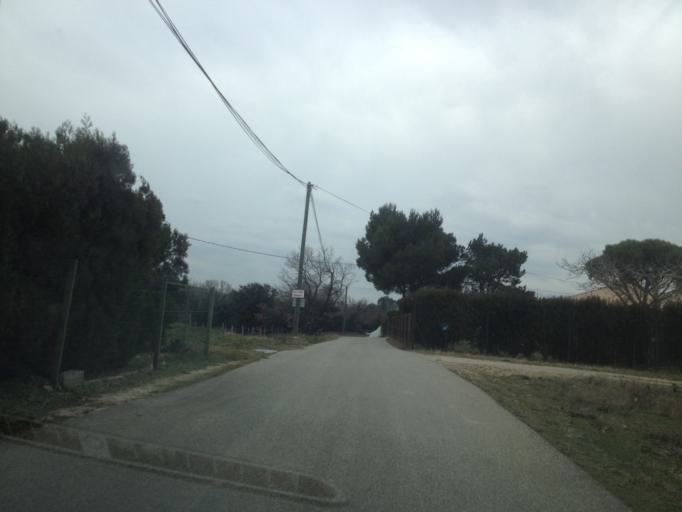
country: FR
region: Provence-Alpes-Cote d'Azur
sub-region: Departement du Vaucluse
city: Bedarrides
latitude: 44.0582
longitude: 4.8910
